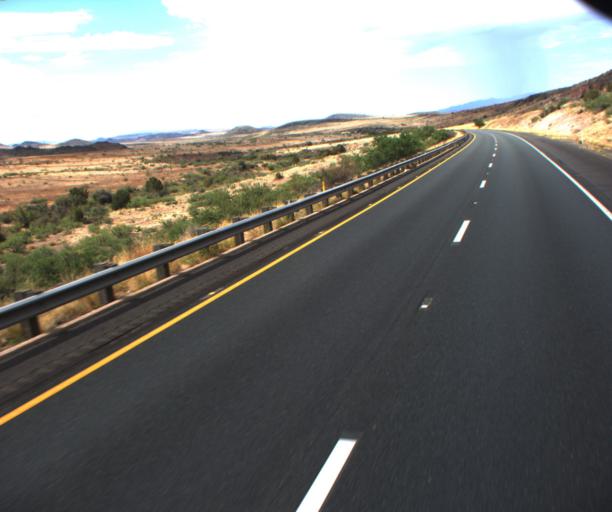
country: US
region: Arizona
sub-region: Yavapai County
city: Cordes Lakes
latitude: 34.4594
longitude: -112.0324
